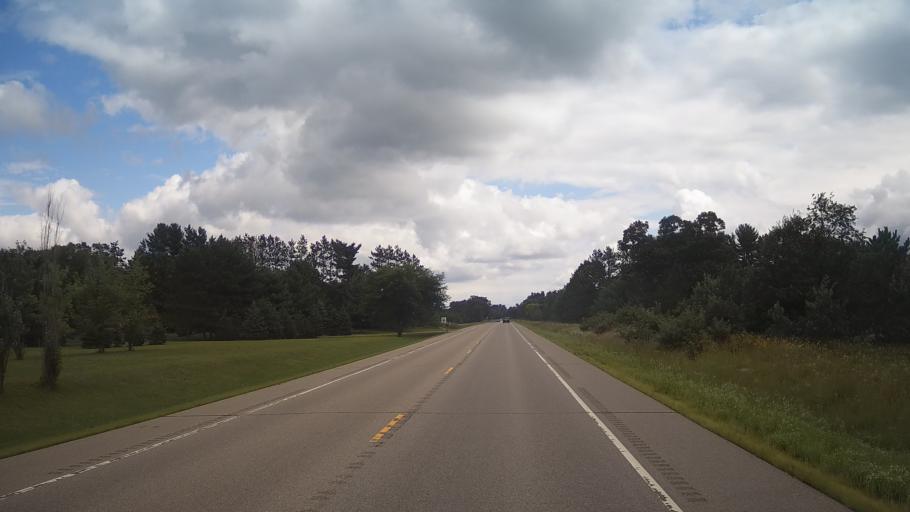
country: US
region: Wisconsin
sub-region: Adams County
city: Friendship
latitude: 44.0236
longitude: -89.6707
